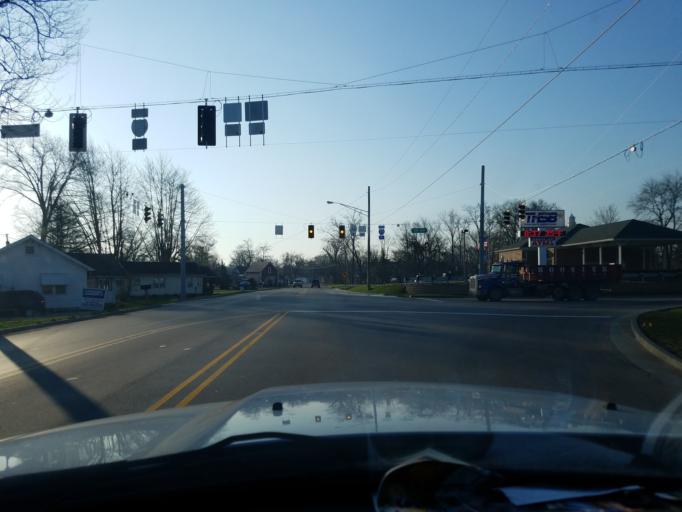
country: US
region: Indiana
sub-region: Vigo County
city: Seelyville
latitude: 39.3918
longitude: -87.3052
